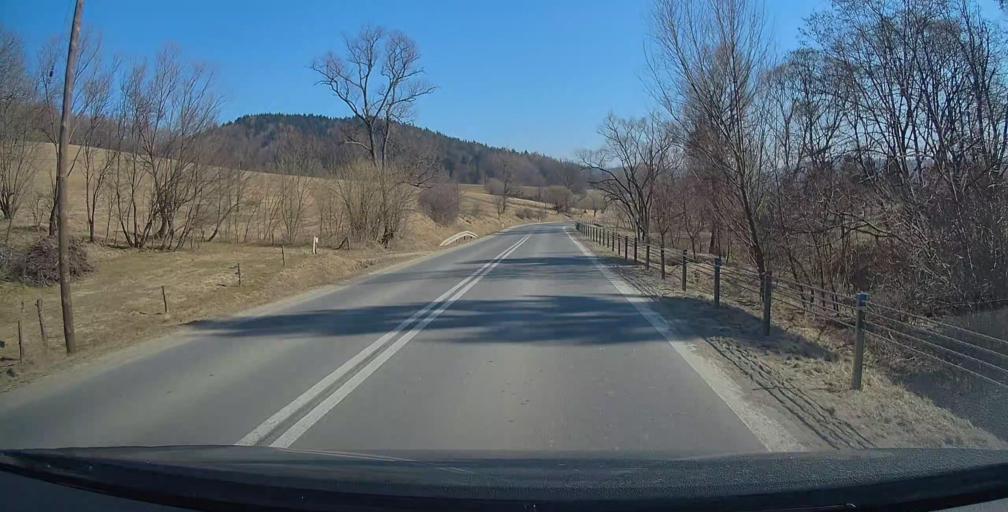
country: PL
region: Subcarpathian Voivodeship
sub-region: Powiat bieszczadzki
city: Ustrzyki Dolne
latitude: 49.4880
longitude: 22.6580
